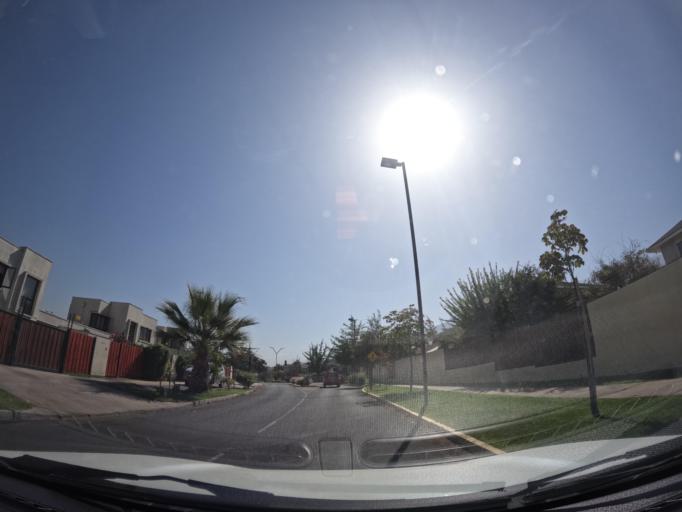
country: CL
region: Santiago Metropolitan
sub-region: Provincia de Santiago
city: Villa Presidente Frei, Nunoa, Santiago, Chile
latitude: -33.4936
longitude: -70.5554
